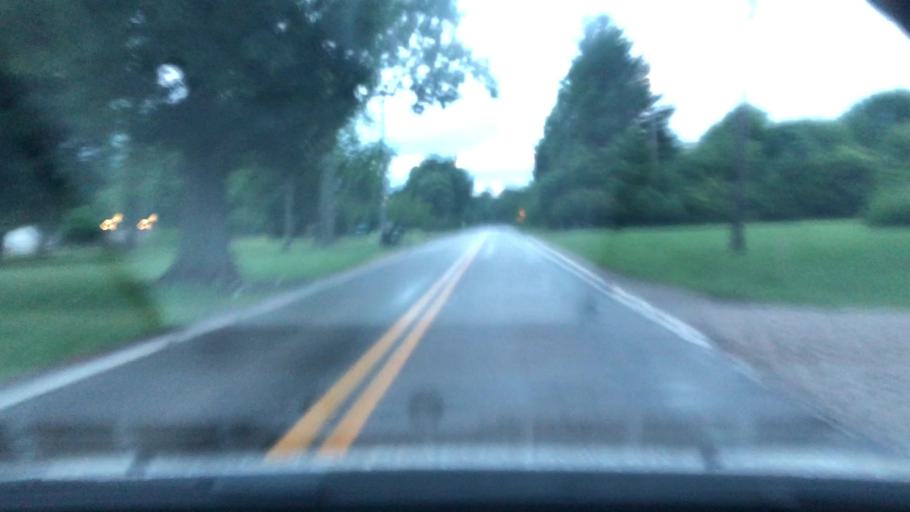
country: US
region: Ohio
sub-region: Franklin County
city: New Albany
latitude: 40.1122
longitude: -82.8574
